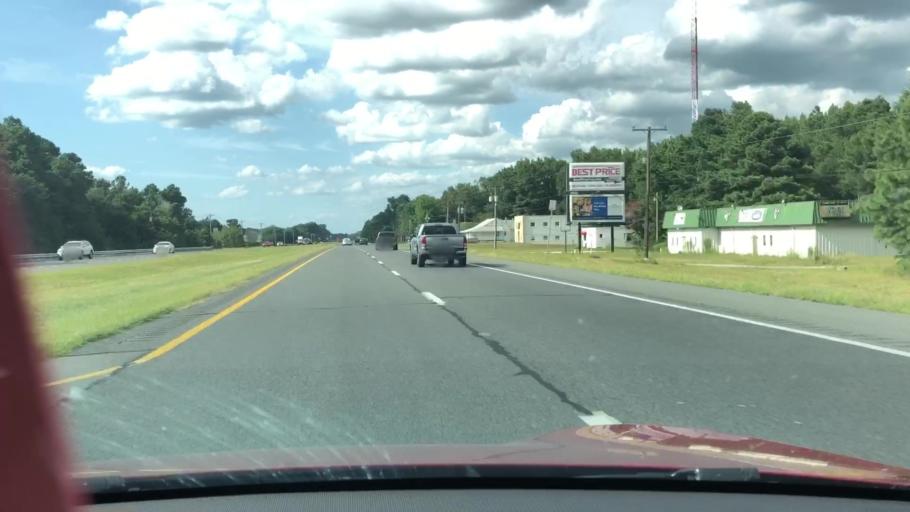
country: US
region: Delaware
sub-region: Sussex County
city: Blades
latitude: 38.6121
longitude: -75.5858
